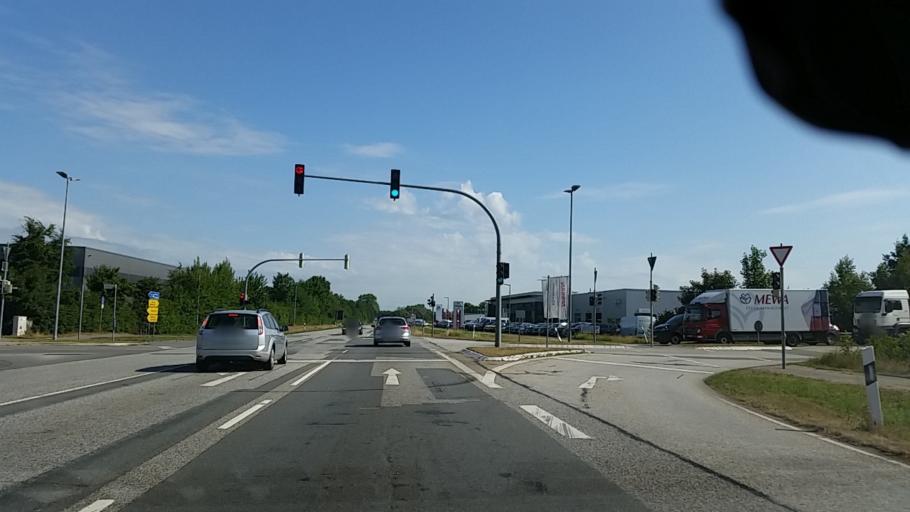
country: DE
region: Schleswig-Holstein
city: Kaltenkirchen
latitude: 53.8168
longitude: 9.9700
